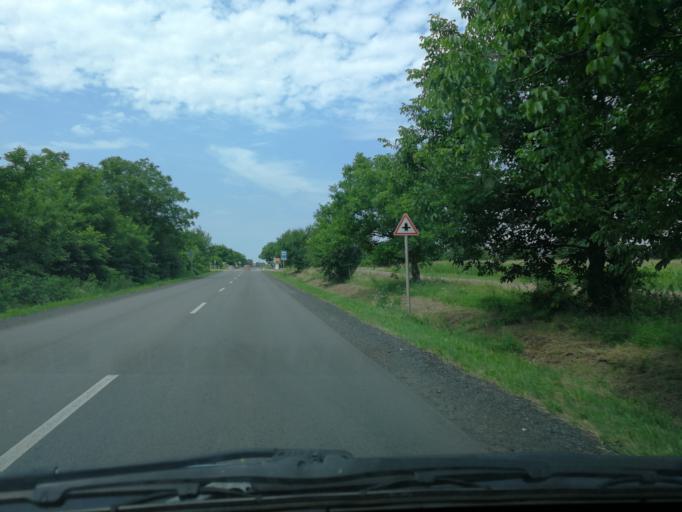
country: HU
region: Baranya
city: Siklos
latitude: 45.8493
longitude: 18.3591
